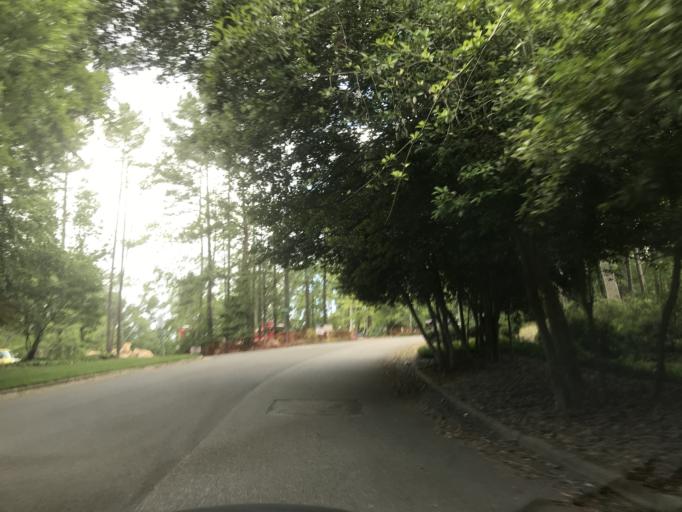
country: US
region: North Carolina
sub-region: Wake County
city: West Raleigh
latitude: 35.8290
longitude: -78.6532
